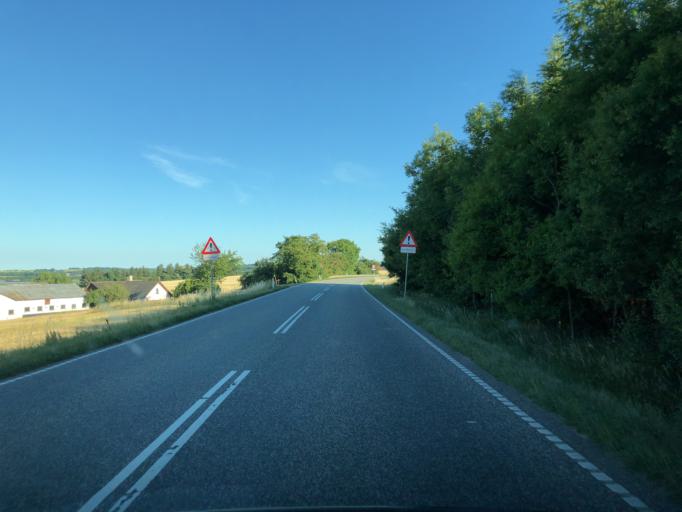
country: DK
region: Central Jutland
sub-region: Skanderborg Kommune
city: Stilling
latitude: 56.0778
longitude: 9.9751
